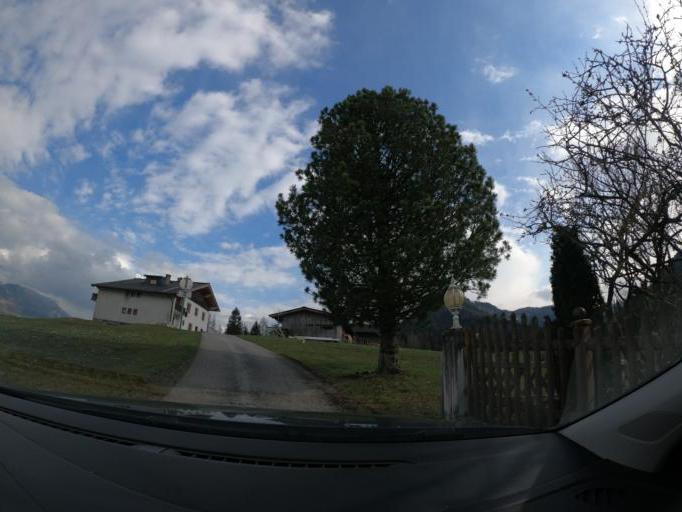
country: AT
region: Salzburg
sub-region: Politischer Bezirk Sankt Johann im Pongau
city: Pfarrwerfen
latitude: 47.4552
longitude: 13.1930
